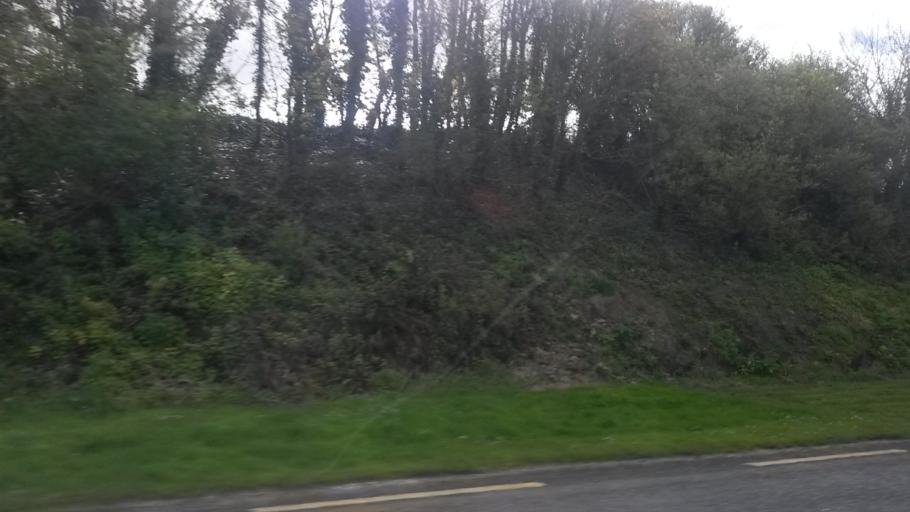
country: IE
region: Munster
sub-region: County Cork
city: Passage West
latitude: 51.8766
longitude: -8.3240
